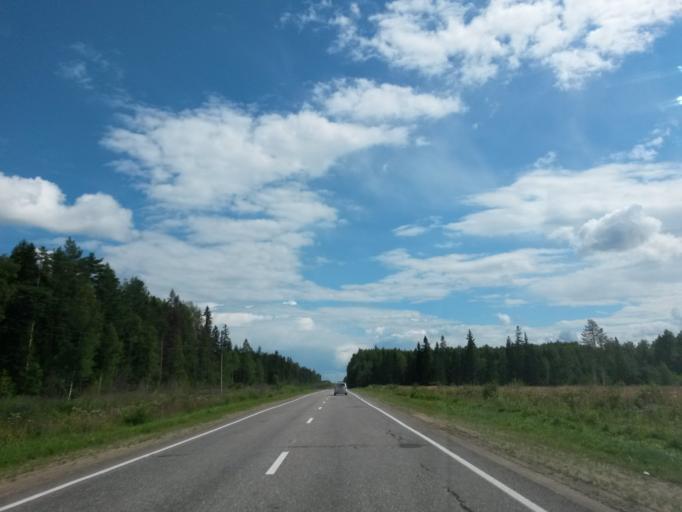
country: RU
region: Jaroslavl
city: Gavrilov-Yam
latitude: 57.2668
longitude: 39.9930
